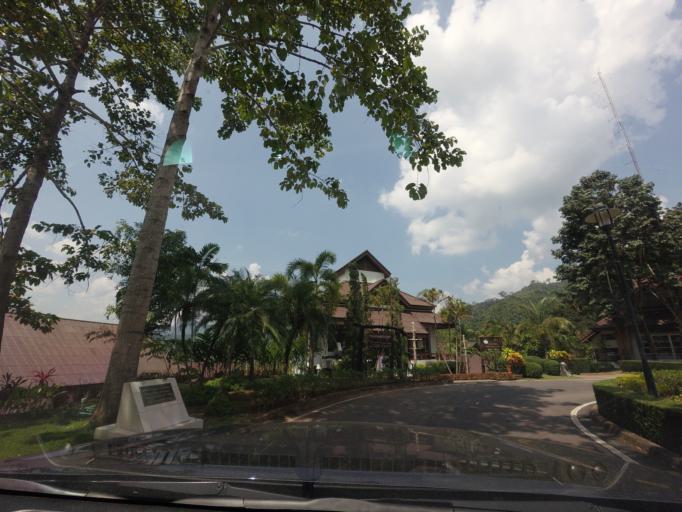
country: TH
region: Nan
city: Bo Kluea
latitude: 19.0248
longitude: 101.2045
